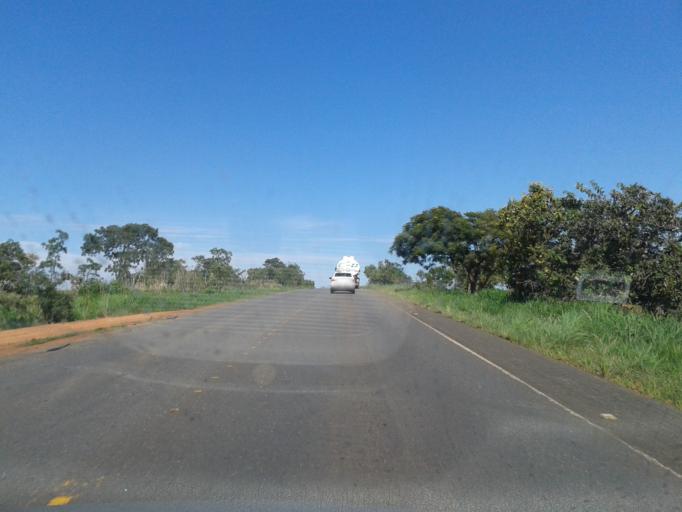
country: BR
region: Goias
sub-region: Bela Vista De Goias
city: Bela Vista de Goias
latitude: -17.0921
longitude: -48.8670
